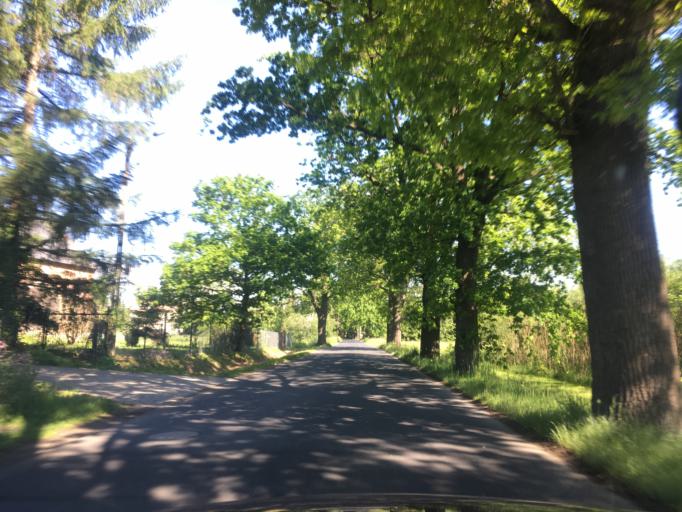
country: PL
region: Lower Silesian Voivodeship
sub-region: Powiat zgorzelecki
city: Sulikow
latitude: 51.0888
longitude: 15.0530
